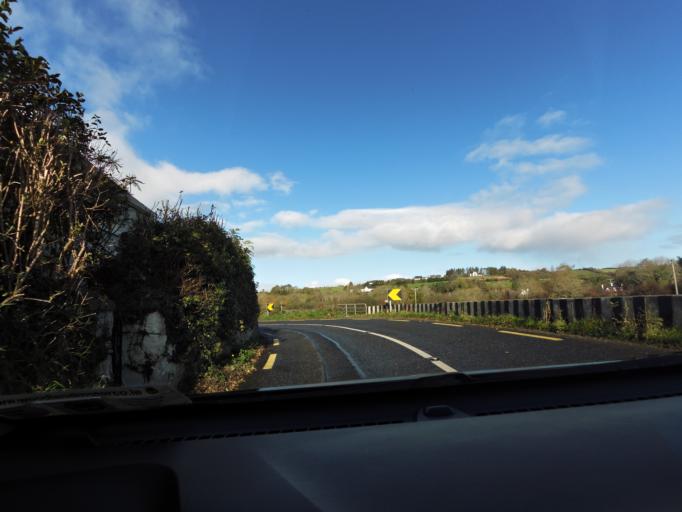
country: IE
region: Connaught
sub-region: Maigh Eo
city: Westport
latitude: 53.8093
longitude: -9.5288
